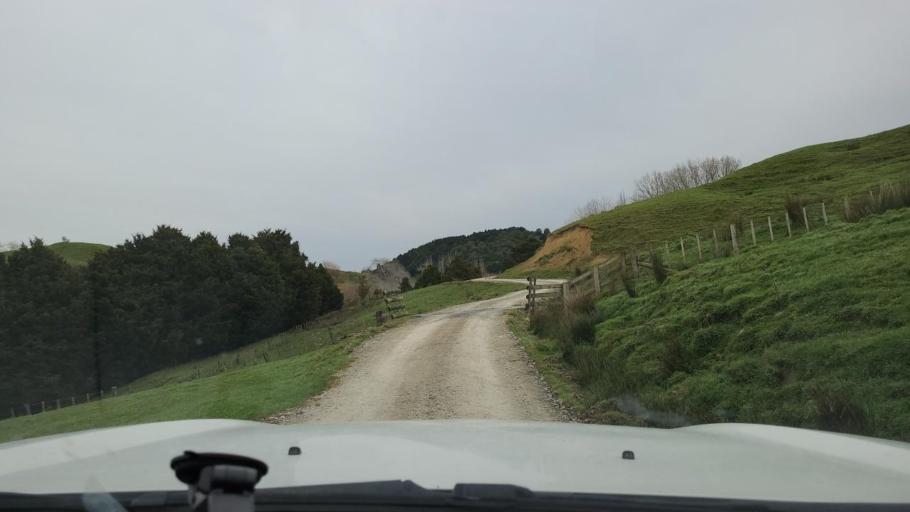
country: NZ
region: Gisborne
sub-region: Gisborne District
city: Gisborne
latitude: -38.4888
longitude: 178.0904
